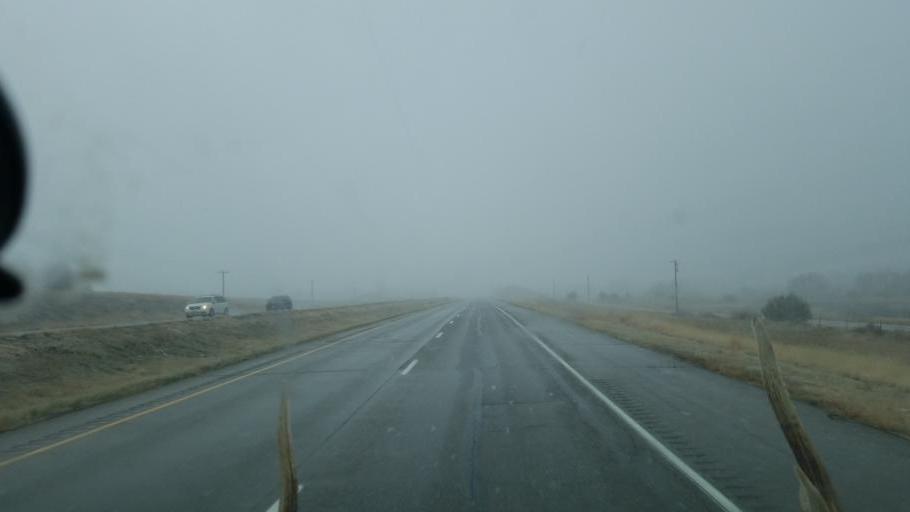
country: US
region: Colorado
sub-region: Pueblo County
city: Colorado City
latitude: 38.0156
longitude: -104.7428
